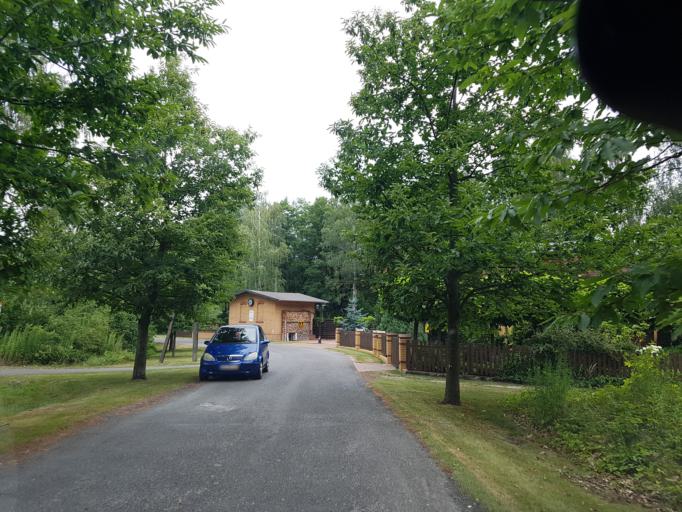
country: DE
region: Brandenburg
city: Sallgast
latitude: 51.5697
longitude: 13.8641
